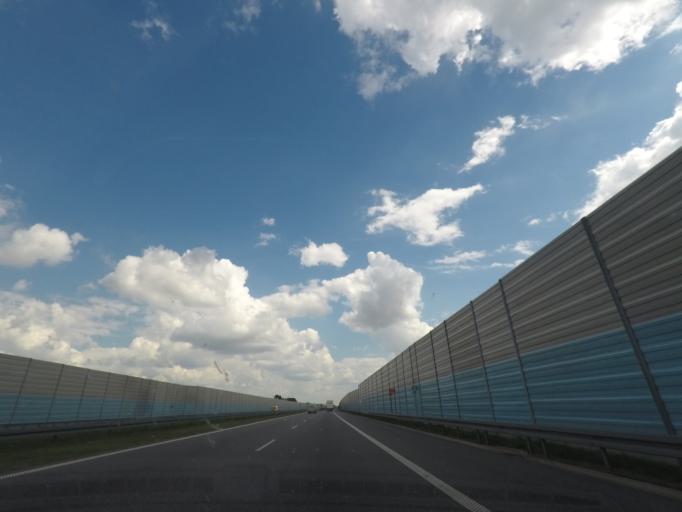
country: PL
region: Lodz Voivodeship
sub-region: powiat Lowicki
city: Lyszkowice
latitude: 51.9922
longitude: 19.9075
